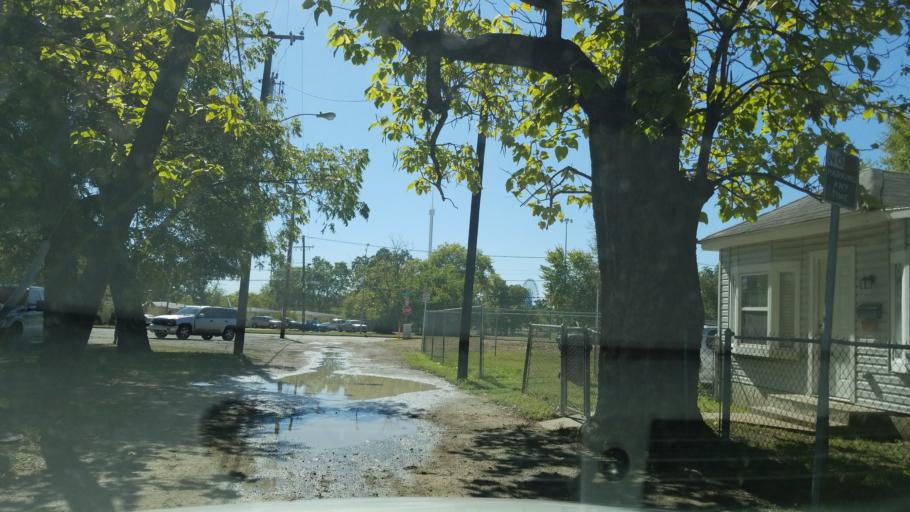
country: US
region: Texas
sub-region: Dallas County
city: Dallas
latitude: 32.7845
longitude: -96.7553
